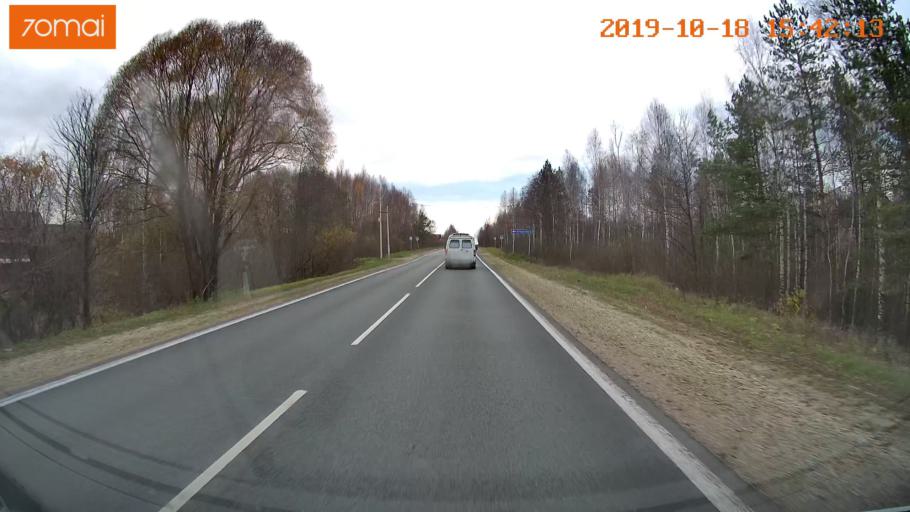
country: RU
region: Vladimir
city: Golovino
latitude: 55.9532
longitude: 40.5713
